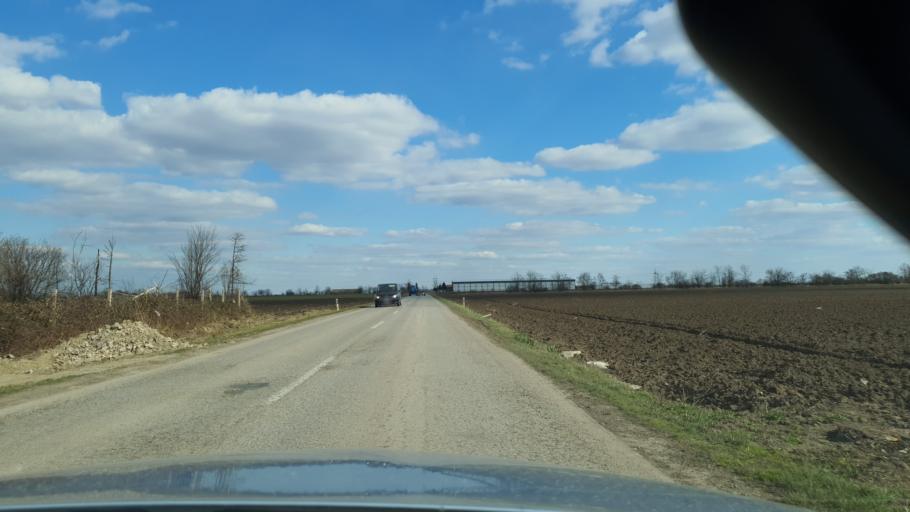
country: RS
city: Zmajevo
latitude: 45.4473
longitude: 19.7105
